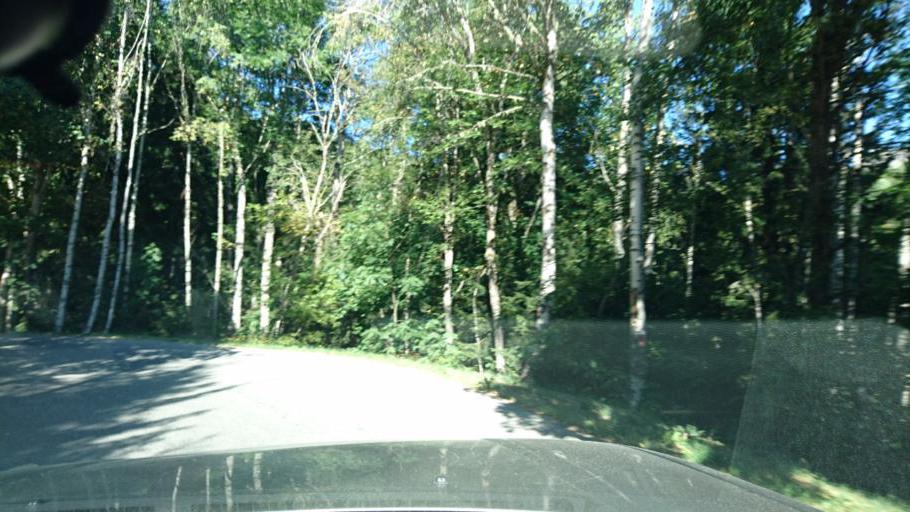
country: IT
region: Aosta Valley
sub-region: Valle d'Aosta
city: Morgex
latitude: 45.7457
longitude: 7.0272
